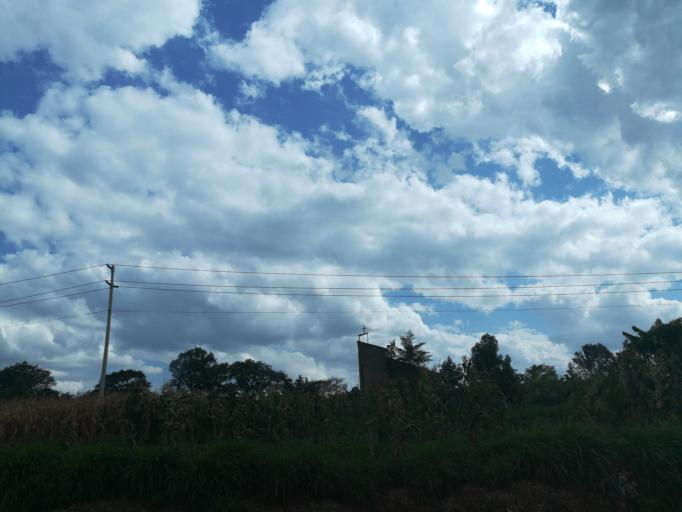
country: KE
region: Nairobi Area
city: Nairobi
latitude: -1.3213
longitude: 36.7911
